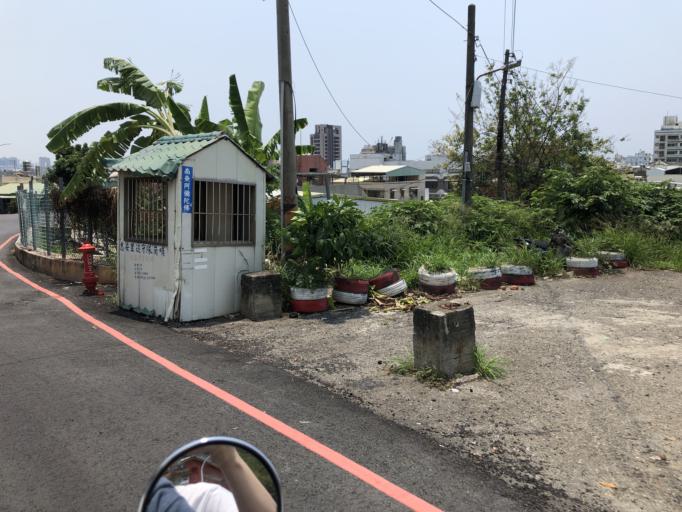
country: TW
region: Kaohsiung
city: Kaohsiung
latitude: 22.6249
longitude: 120.2731
